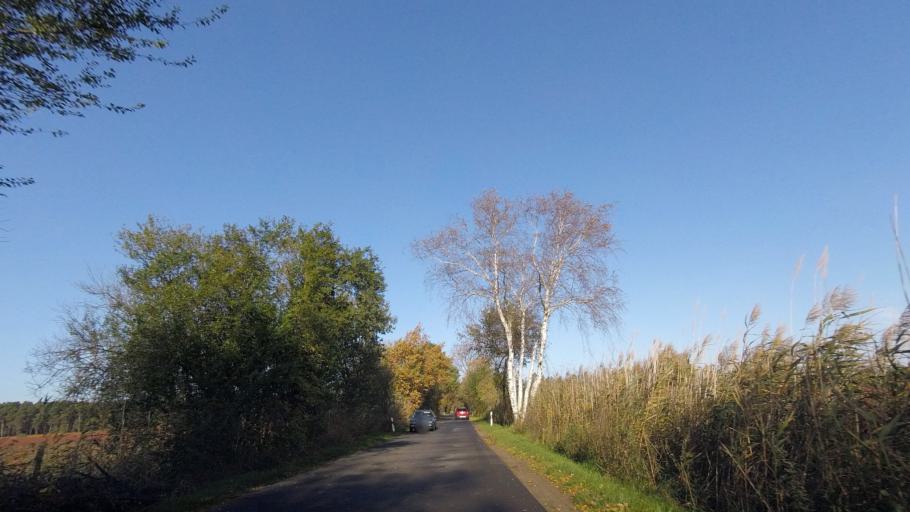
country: DE
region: Brandenburg
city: Borkheide
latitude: 52.2014
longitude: 12.9033
